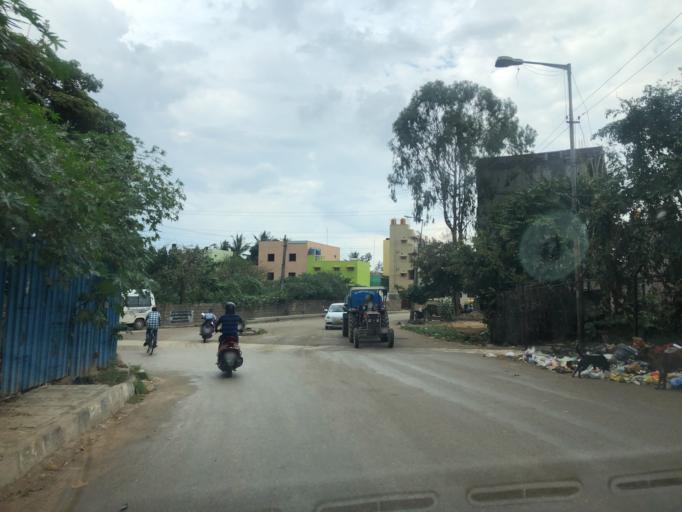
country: IN
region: Karnataka
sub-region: Bangalore Urban
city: Bangalore
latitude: 12.9874
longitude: 77.6973
